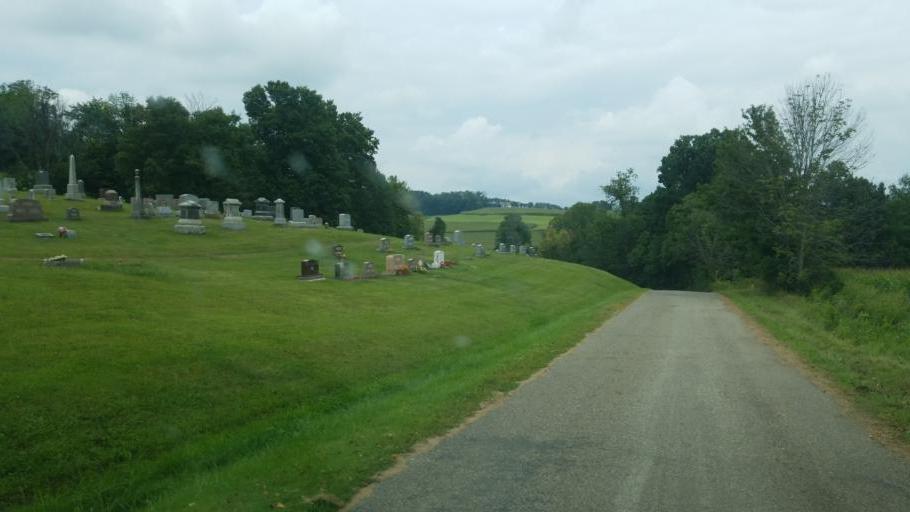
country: US
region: Ohio
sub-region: Knox County
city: Danville
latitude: 40.5048
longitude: -82.3051
